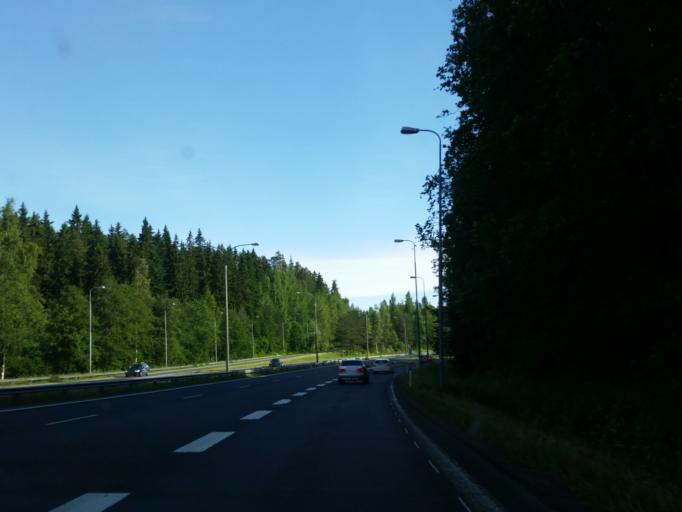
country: FI
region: Northern Savo
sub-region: Kuopio
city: Kuopio
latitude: 62.9100
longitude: 27.6868
